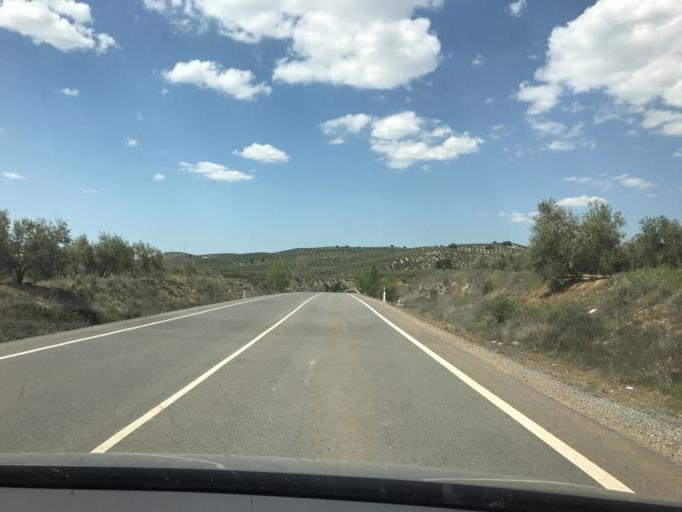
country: ES
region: Andalusia
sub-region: Provincia de Jaen
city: Frailes
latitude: 37.4345
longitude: -3.8064
